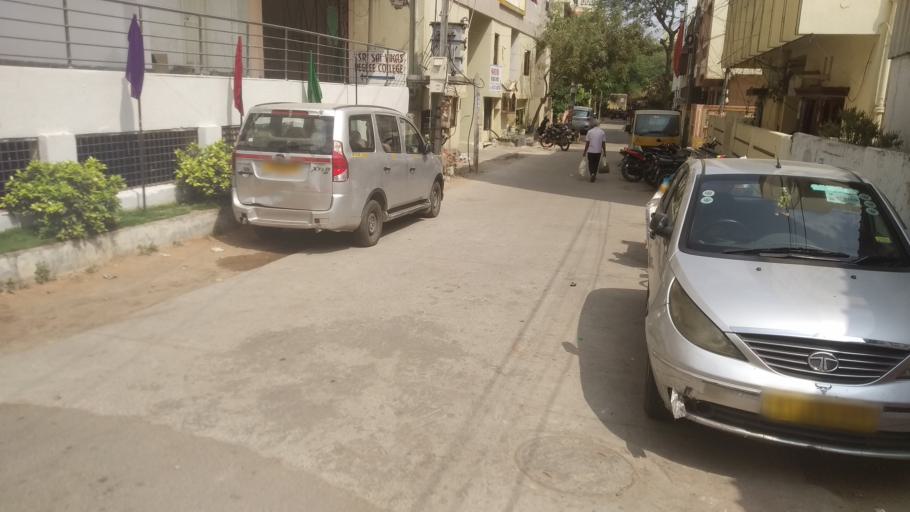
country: IN
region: Telangana
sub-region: Rangareddi
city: Gaddi Annaram
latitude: 17.3455
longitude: 78.5090
